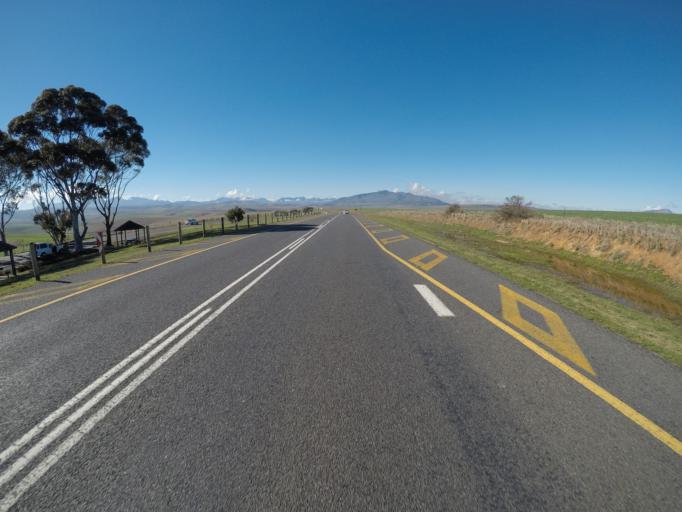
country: ZA
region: Western Cape
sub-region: Overberg District Municipality
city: Caledon
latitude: -34.2219
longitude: 19.3060
